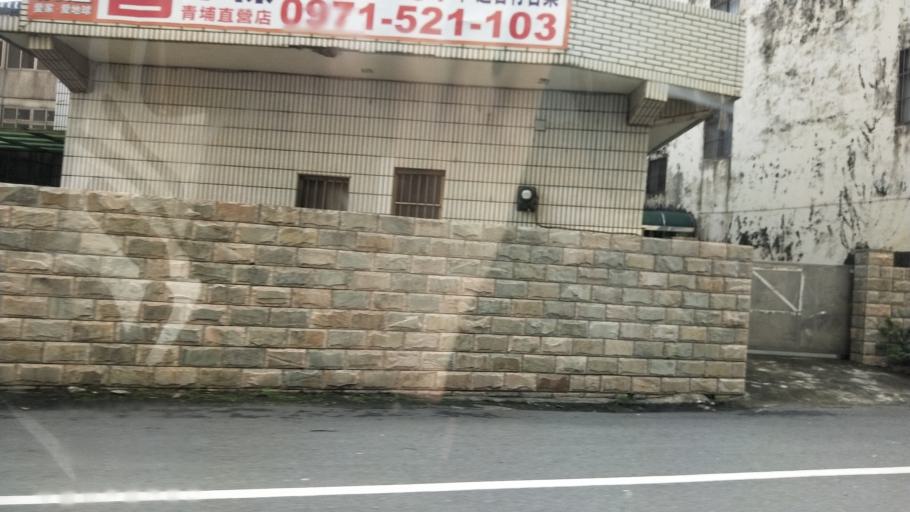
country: TW
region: Taiwan
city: Taoyuan City
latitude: 25.0154
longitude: 121.1342
